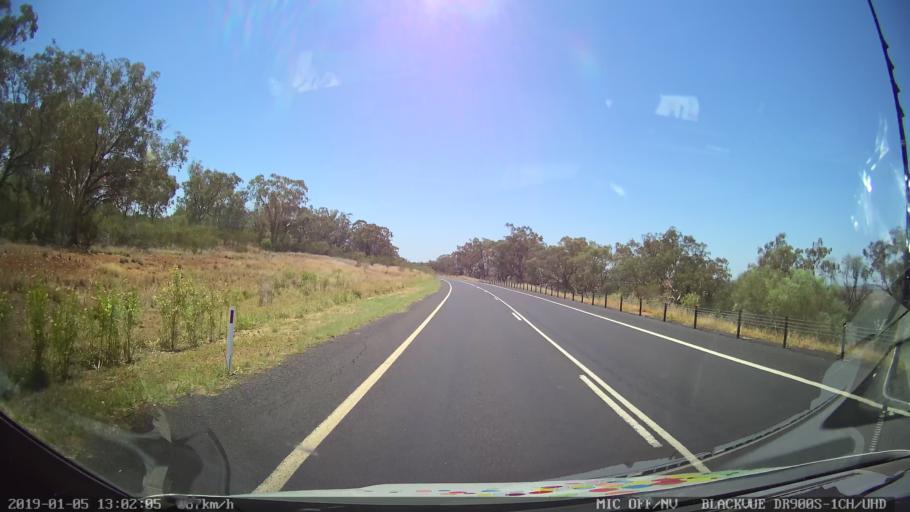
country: AU
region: New South Wales
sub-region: Narrabri
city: Boggabri
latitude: -31.1165
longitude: 149.8065
